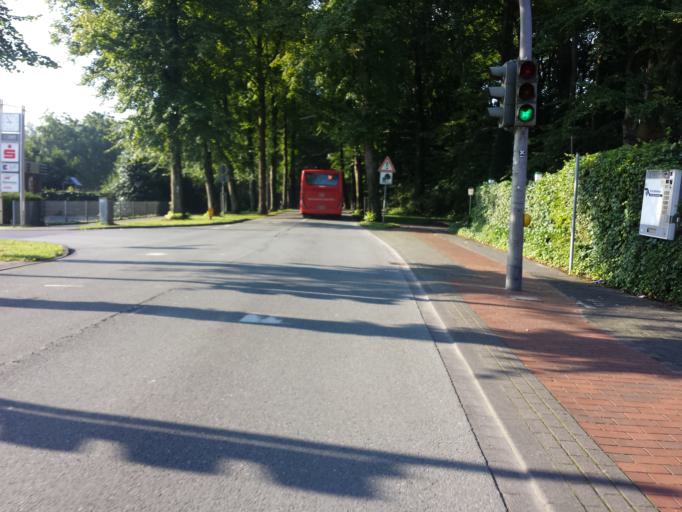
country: DE
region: North Rhine-Westphalia
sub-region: Regierungsbezirk Detmold
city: Harsewinkel
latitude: 51.9496
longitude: 8.2787
